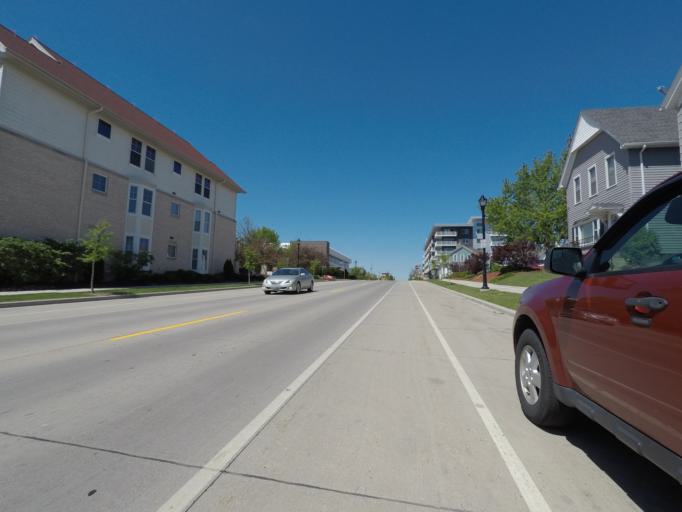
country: US
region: Wisconsin
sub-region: Sheboygan County
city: Sheboygan
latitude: 43.7498
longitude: -87.7087
